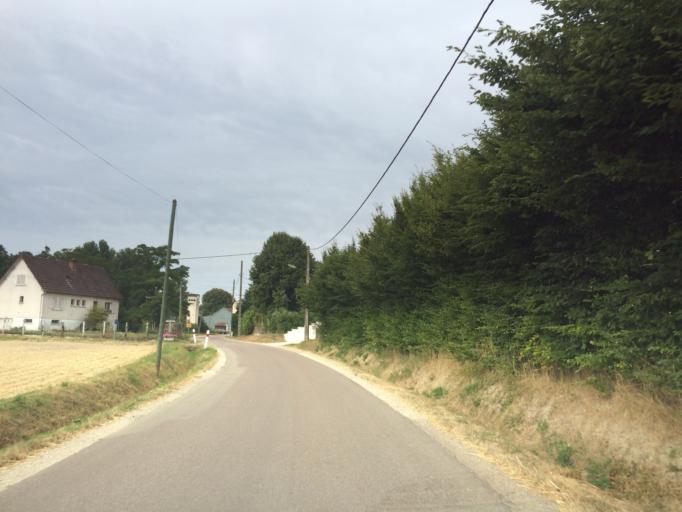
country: FR
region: Bourgogne
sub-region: Departement de l'Yonne
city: Aillant-sur-Tholon
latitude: 47.8524
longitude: 3.3360
